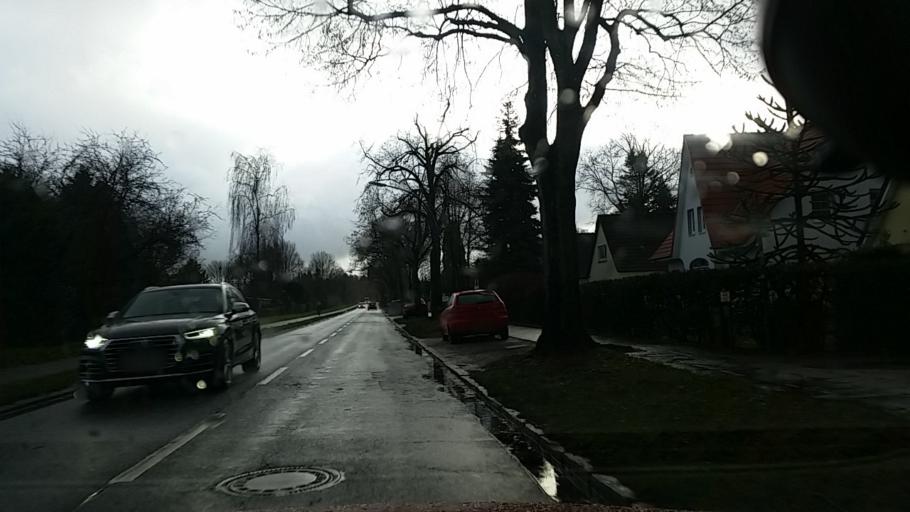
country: DE
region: Schleswig-Holstein
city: Halstenbek
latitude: 53.5823
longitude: 9.8227
